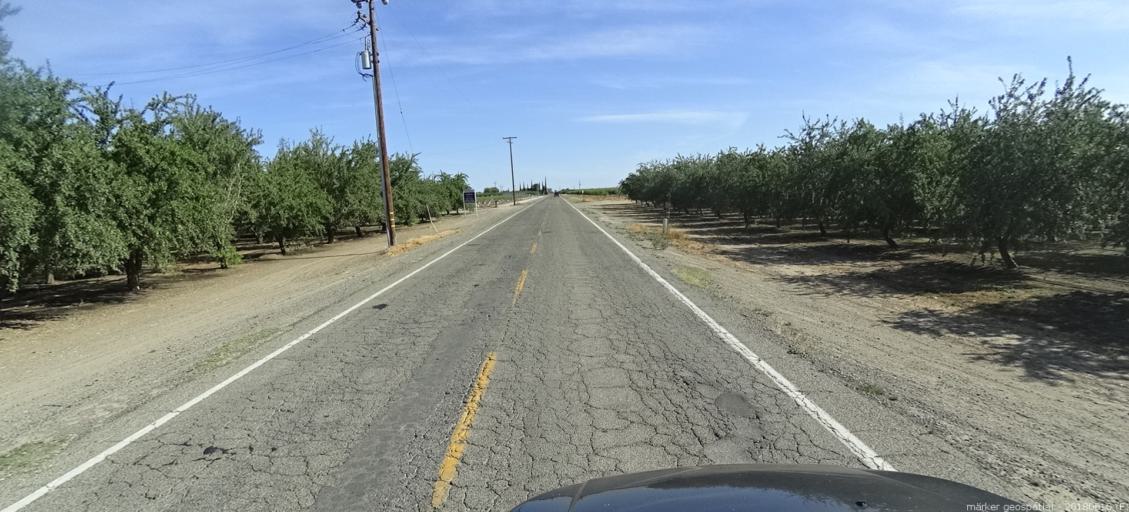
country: US
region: California
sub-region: Madera County
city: Chowchilla
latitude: 37.0647
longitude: -120.2568
